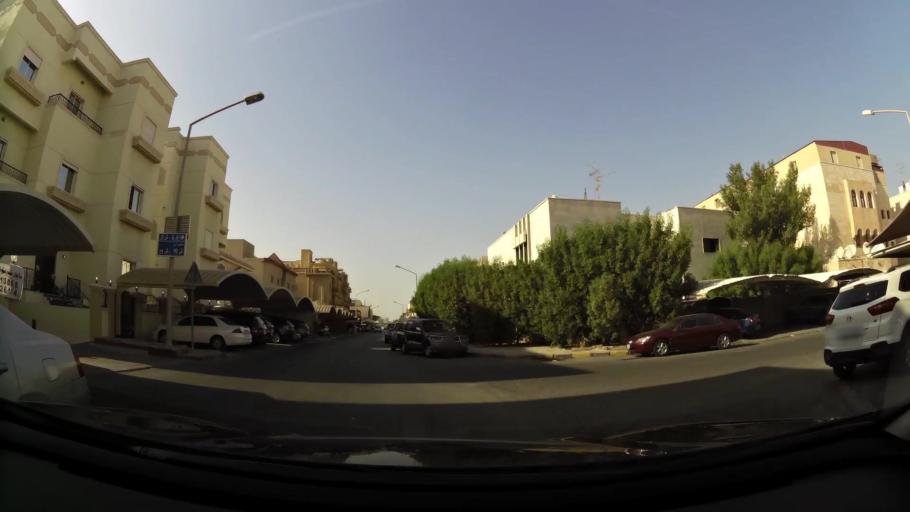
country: KW
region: Muhafazat Hawalli
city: Salwa
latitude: 29.2990
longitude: 48.0668
